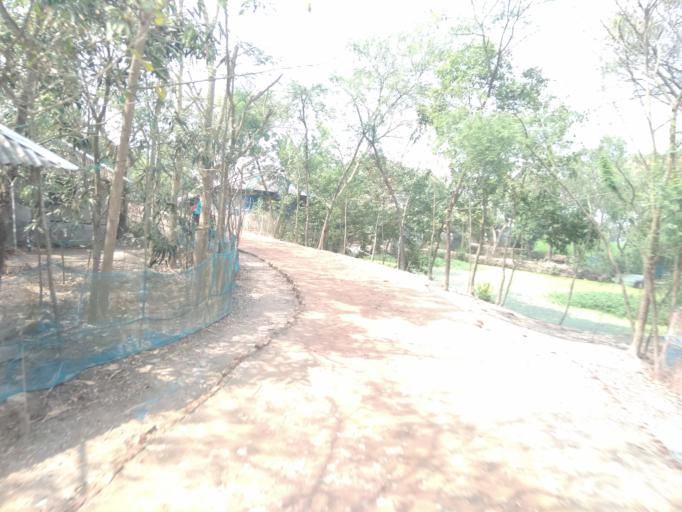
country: IN
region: West Bengal
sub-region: North 24 Parganas
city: Taki
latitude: 22.2997
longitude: 89.2695
